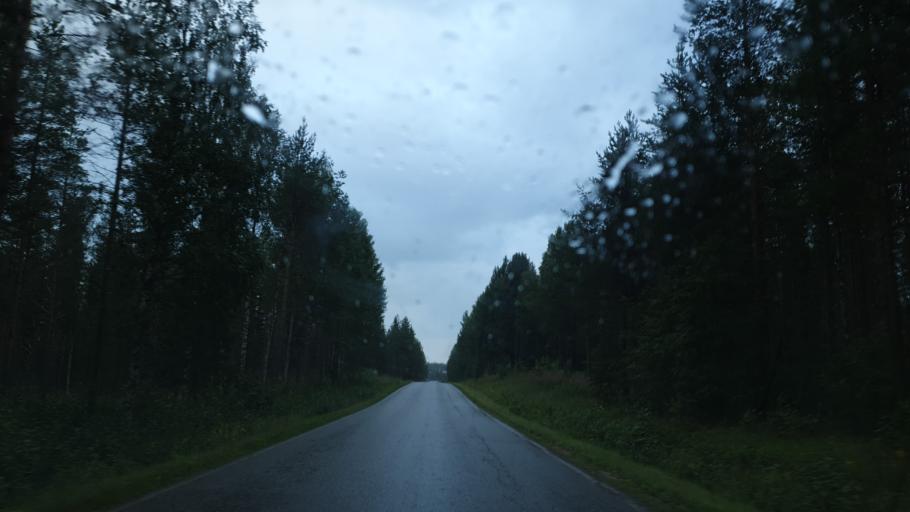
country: FI
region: Kainuu
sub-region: Kehys-Kainuu
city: Kuhmo
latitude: 64.1610
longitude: 29.3756
